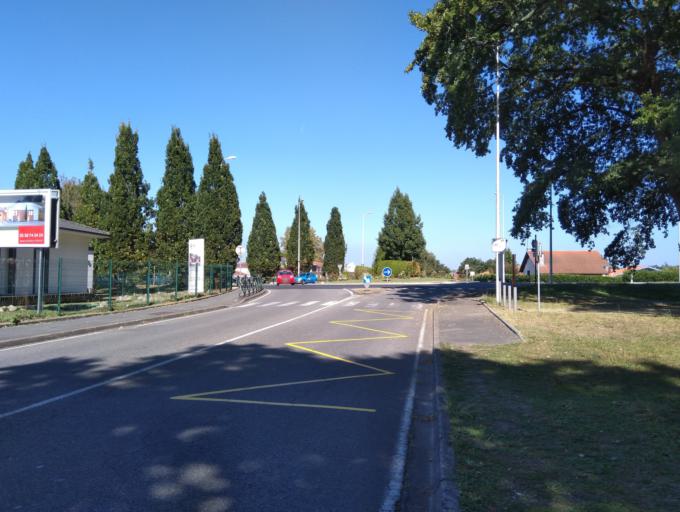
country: FR
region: Aquitaine
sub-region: Departement des Landes
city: Dax
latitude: 43.7018
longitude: -1.0324
